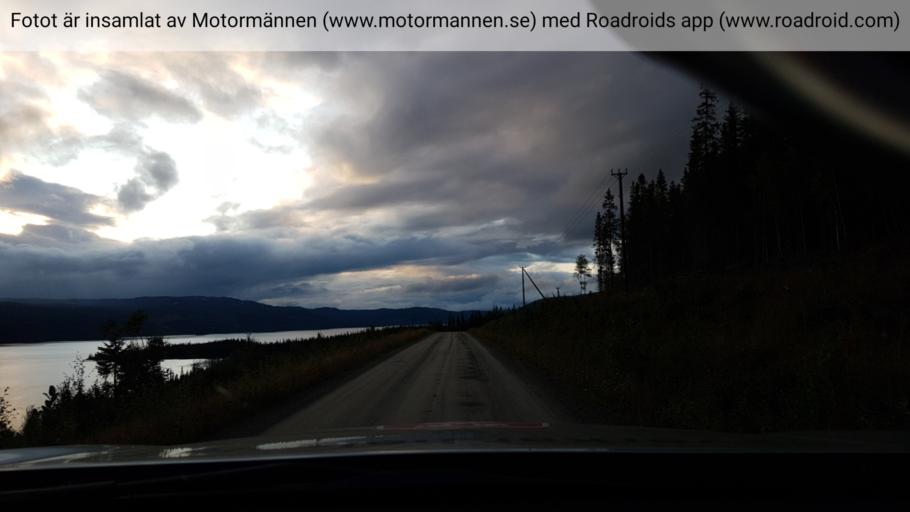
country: SE
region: Vaesterbotten
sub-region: Vilhelmina Kommun
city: Sjoberg
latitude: 65.5859
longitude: 15.2918
